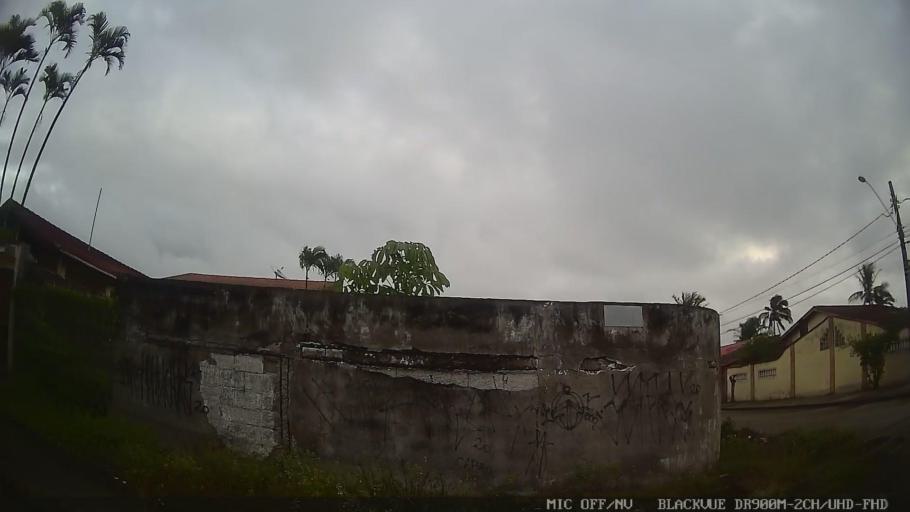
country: BR
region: Sao Paulo
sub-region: Itanhaem
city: Itanhaem
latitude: -24.2150
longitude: -46.8487
